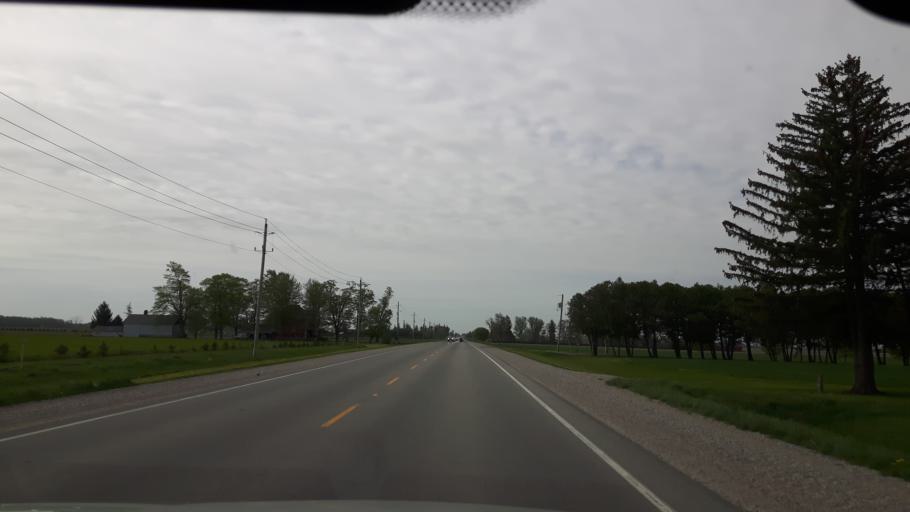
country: CA
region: Ontario
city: South Huron
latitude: 43.3875
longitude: -81.4890
